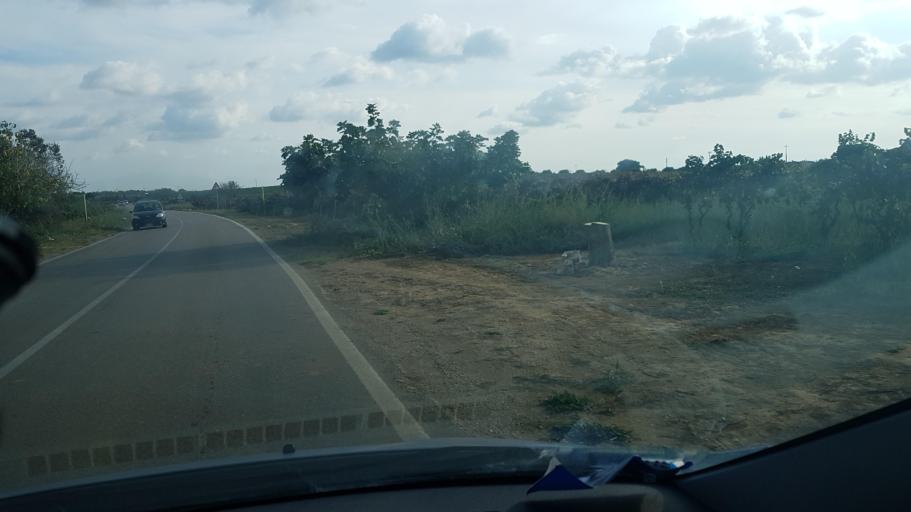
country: IT
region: Apulia
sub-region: Provincia di Lecce
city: Guagnano
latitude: 40.4282
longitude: 17.9497
